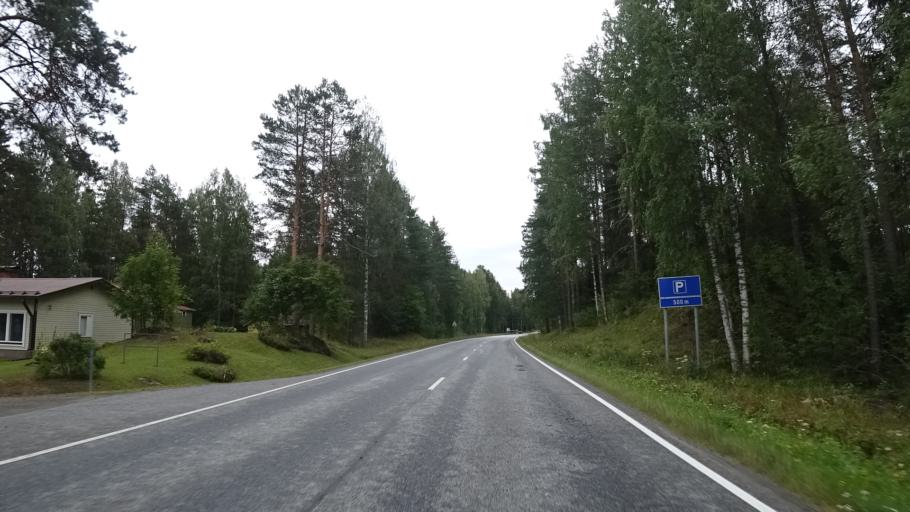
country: FI
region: North Karelia
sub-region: Keski-Karjala
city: Kesaelahti
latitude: 62.0945
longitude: 29.8657
